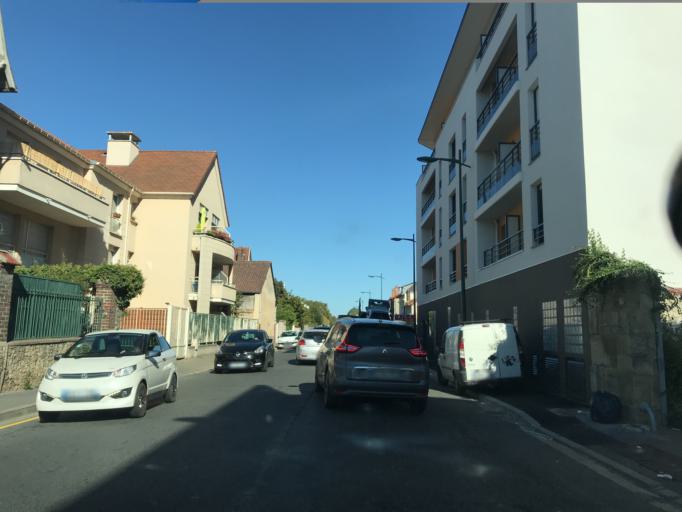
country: FR
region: Ile-de-France
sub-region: Departement du Val-d'Oise
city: Pontoise
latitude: 49.0478
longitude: 2.1050
